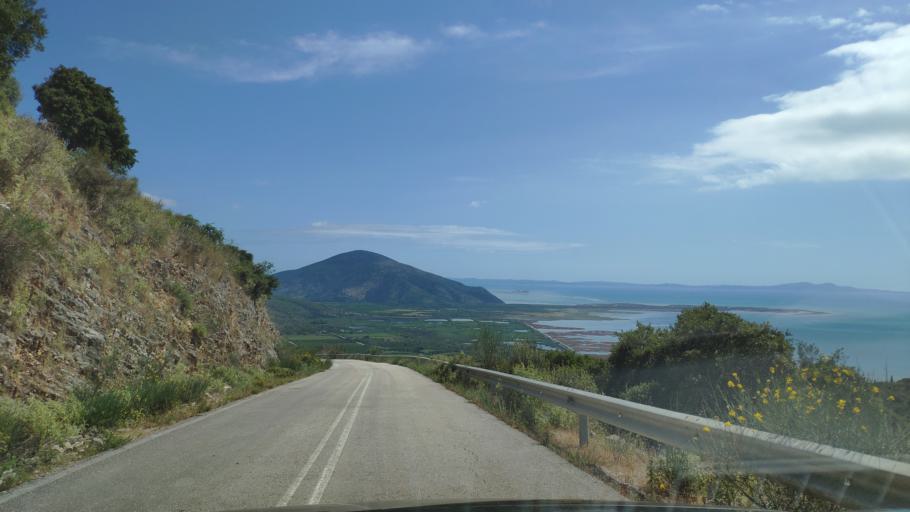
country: AL
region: Vlore
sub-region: Rrethi i Sarandes
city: Konispol
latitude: 39.6347
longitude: 20.2059
